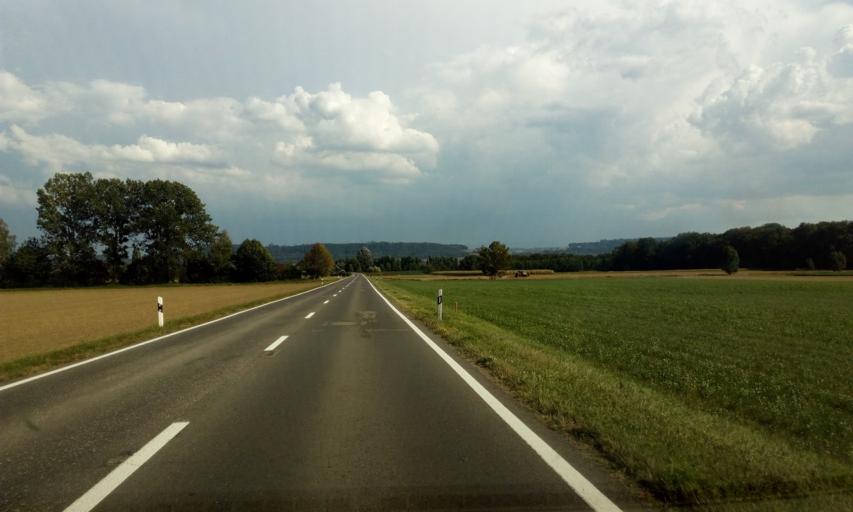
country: CH
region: Fribourg
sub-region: Broye District
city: Domdidier
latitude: 46.8936
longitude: 7.0030
